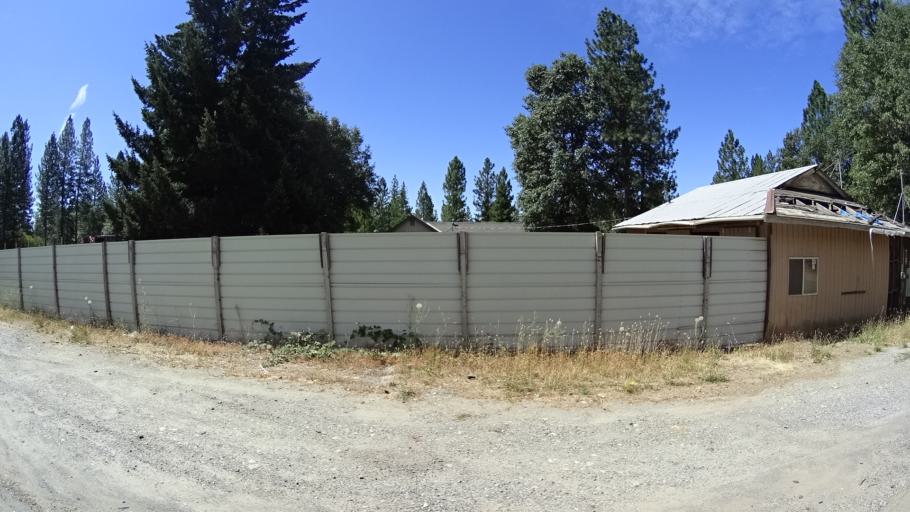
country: US
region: California
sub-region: Amador County
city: Pioneer
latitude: 38.3359
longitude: -120.5338
